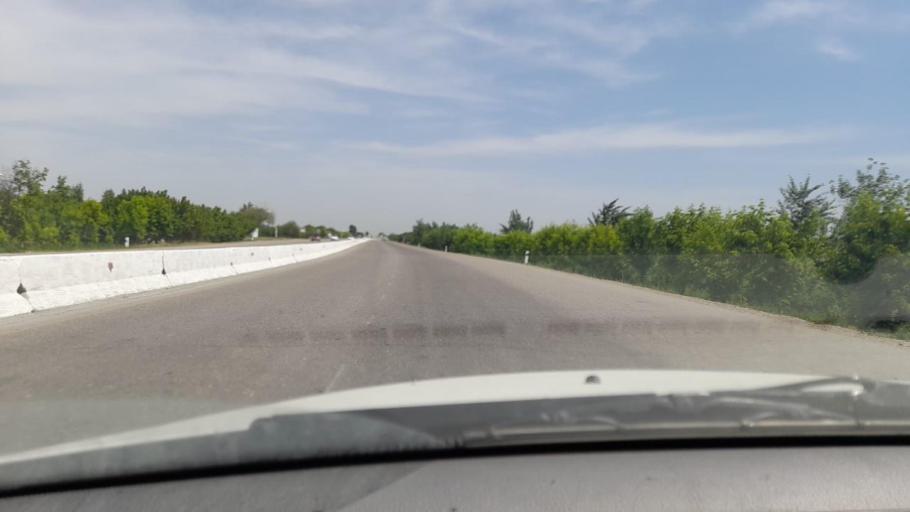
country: UZ
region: Bukhara
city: Galaosiyo
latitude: 39.8711
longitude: 64.4548
